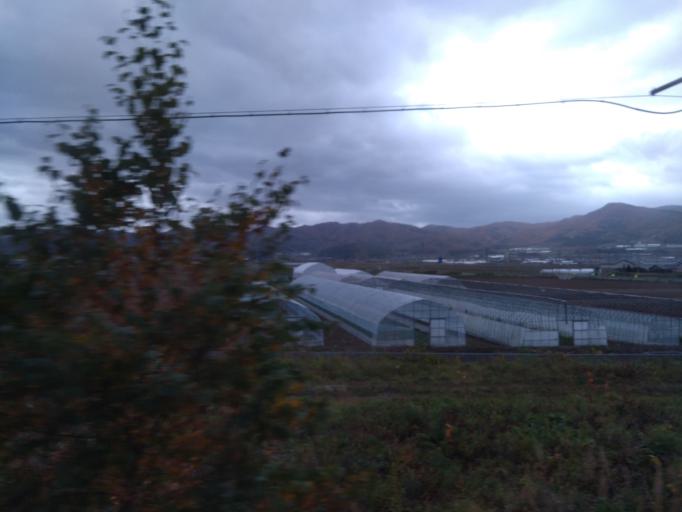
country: JP
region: Hokkaido
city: Nanae
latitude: 41.9037
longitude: 140.6532
